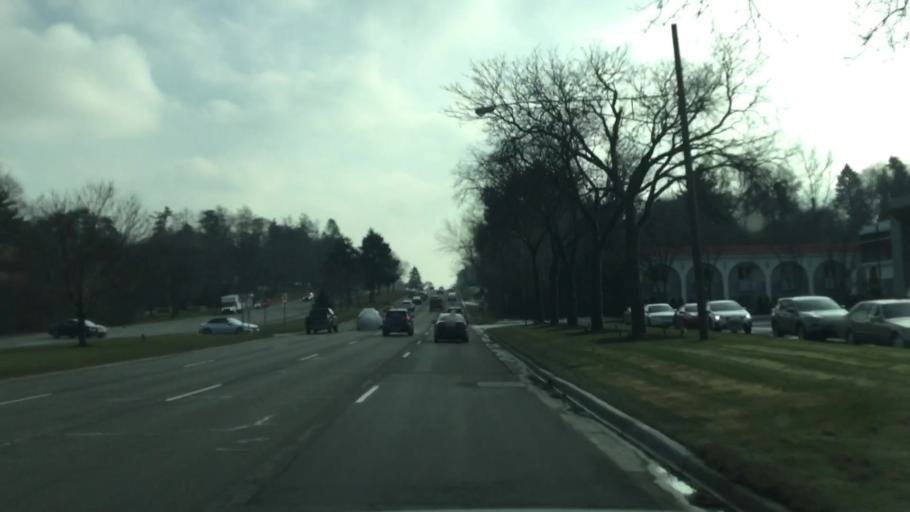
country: US
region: Michigan
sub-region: Oakland County
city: Bloomfield Hills
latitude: 42.5816
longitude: -83.2436
